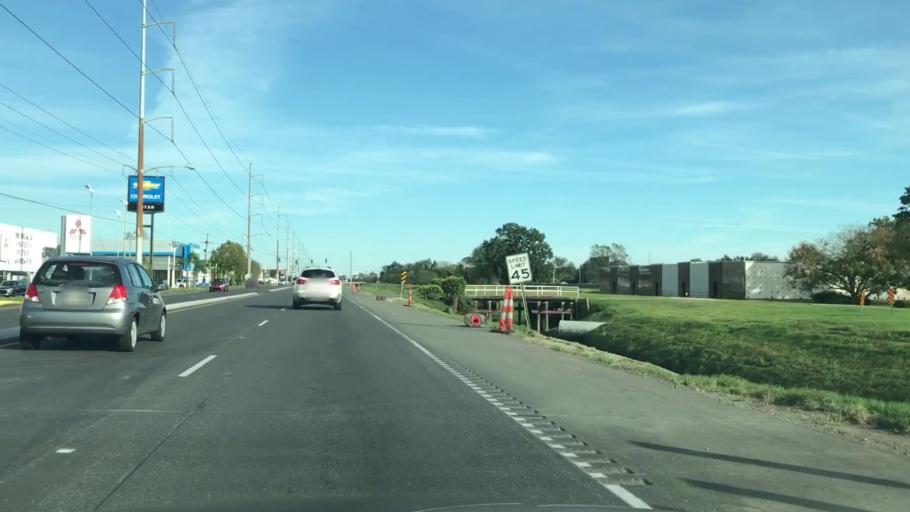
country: US
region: Louisiana
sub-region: Jefferson Parish
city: Kenner
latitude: 29.9789
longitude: -90.2287
